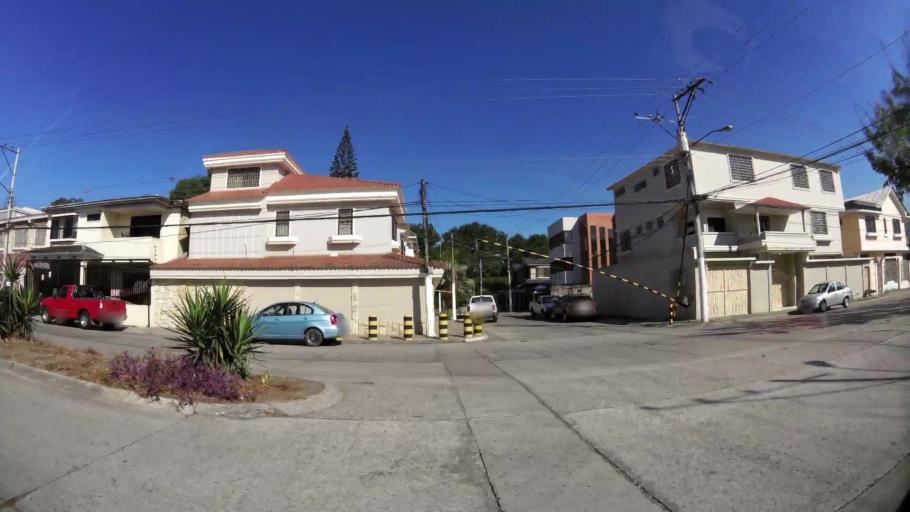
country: EC
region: Guayas
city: Guayaquil
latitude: -2.1557
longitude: -79.9020
